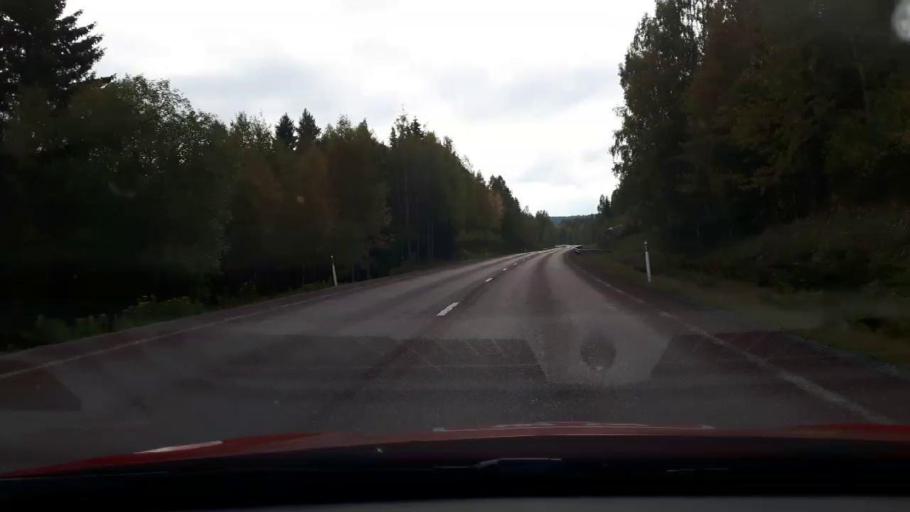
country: SE
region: Gaevleborg
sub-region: Ljusdals Kommun
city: Jaervsoe
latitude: 61.6136
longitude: 16.2954
